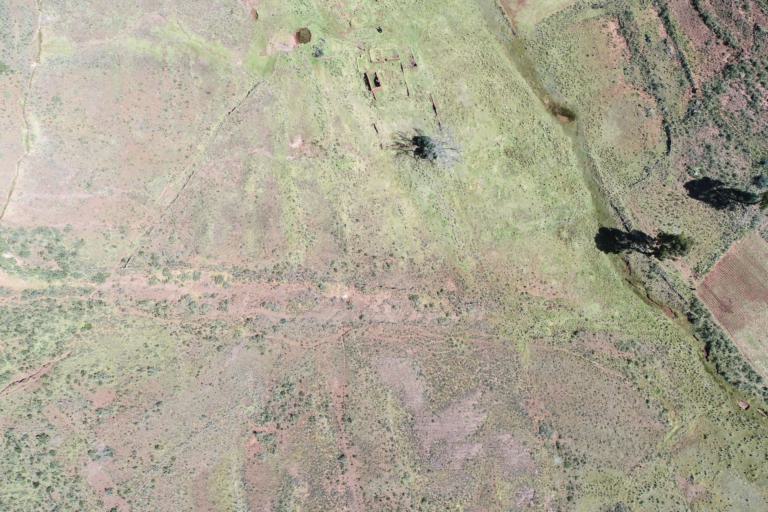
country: BO
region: La Paz
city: Tiahuanaco
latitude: -16.6078
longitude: -68.7738
